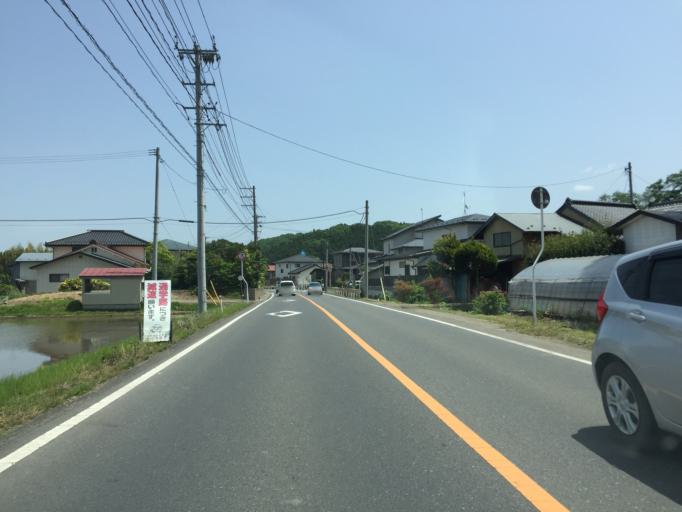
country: JP
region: Fukushima
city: Ishikawa
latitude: 37.1142
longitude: 140.2586
